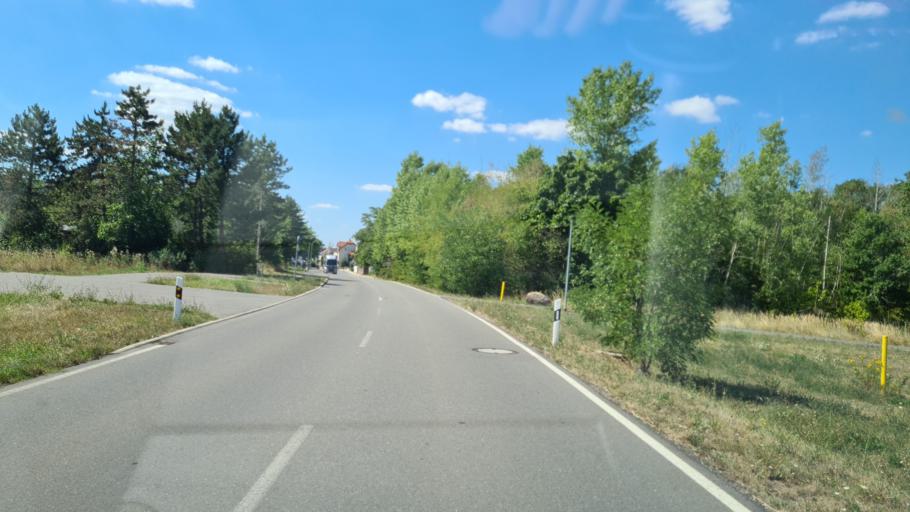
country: DE
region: Saxony
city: Borna
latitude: 51.1297
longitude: 12.5111
